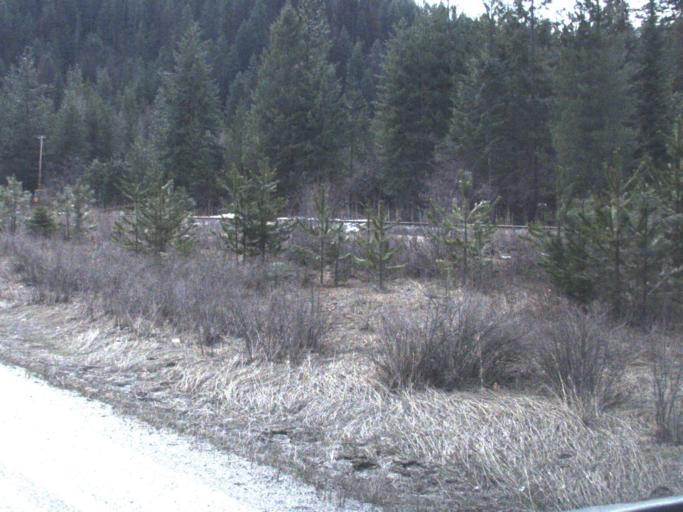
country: US
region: Washington
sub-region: Stevens County
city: Chewelah
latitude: 48.5561
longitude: -117.3466
